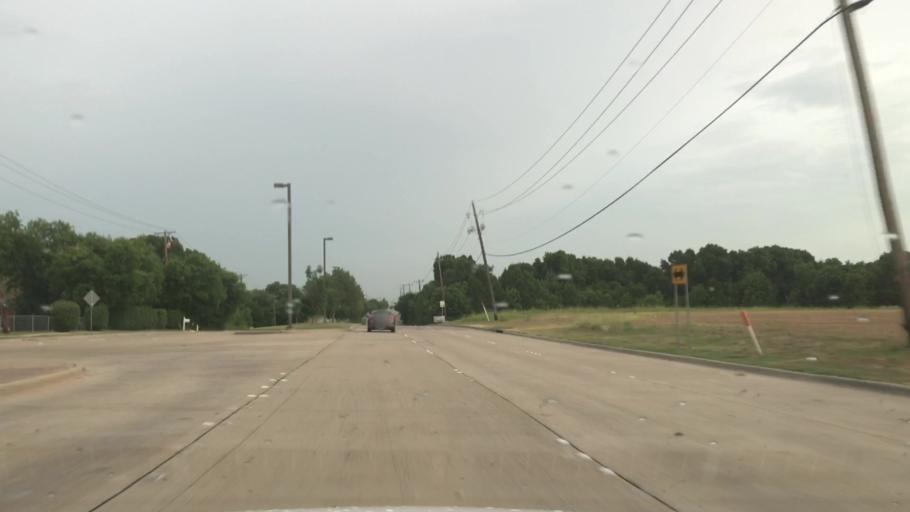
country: US
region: Texas
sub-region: Dallas County
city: Mesquite
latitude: 32.7303
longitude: -96.5539
